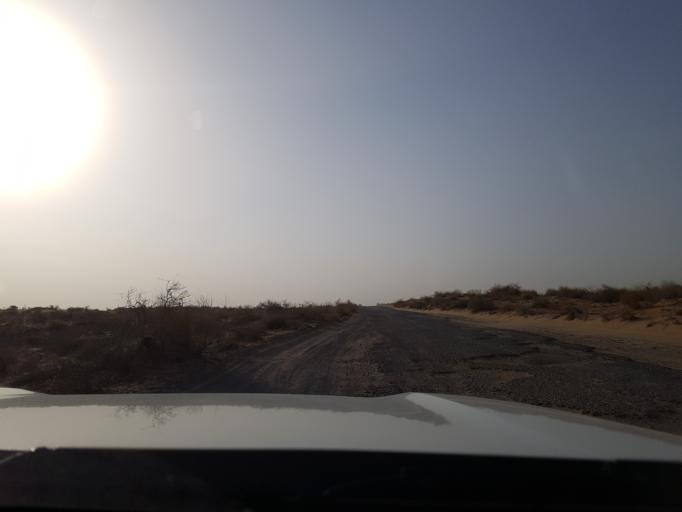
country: UZ
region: Xorazm
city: Hazorasp
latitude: 41.1934
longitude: 60.9100
